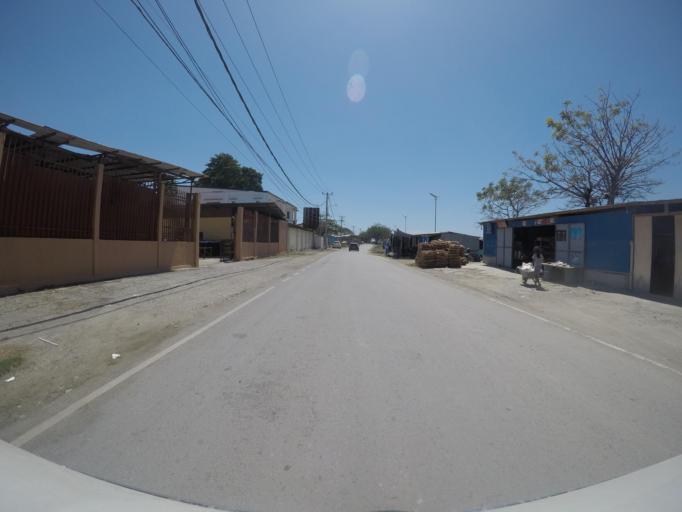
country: TL
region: Dili
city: Dili
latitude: -8.5425
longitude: 125.5452
